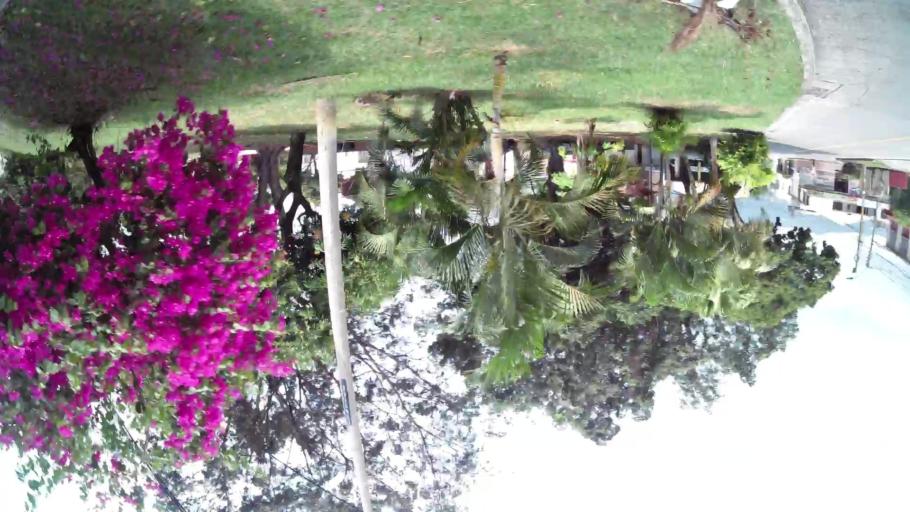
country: CO
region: Valle del Cauca
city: Cali
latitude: 3.4843
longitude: -76.5084
